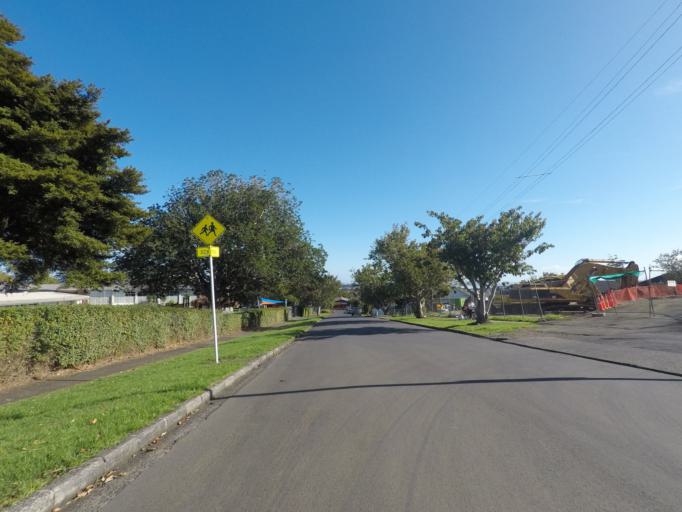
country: NZ
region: Auckland
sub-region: Auckland
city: Rosebank
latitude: -36.8893
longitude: 174.7128
